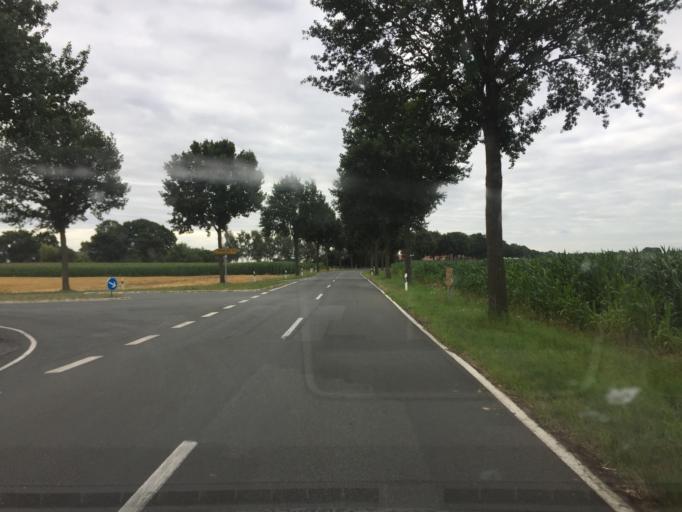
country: DE
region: Lower Saxony
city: Ehrenburg
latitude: 52.7638
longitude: 8.7166
